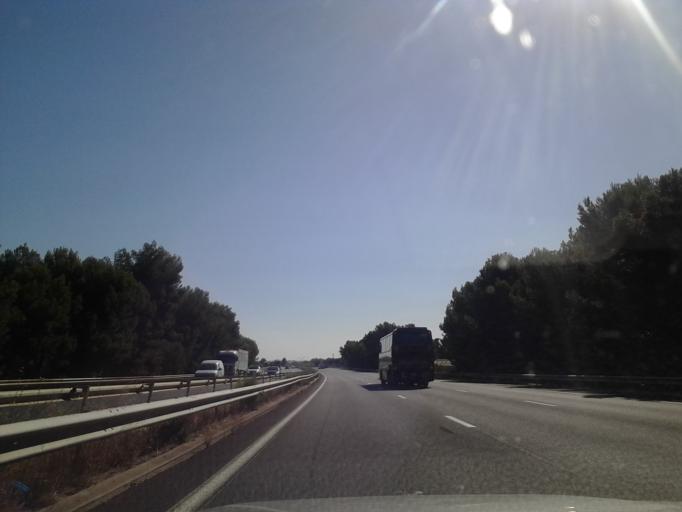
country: FR
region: Languedoc-Roussillon
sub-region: Departement de l'Aude
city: Fleury
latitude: 43.2312
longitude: 3.1250
